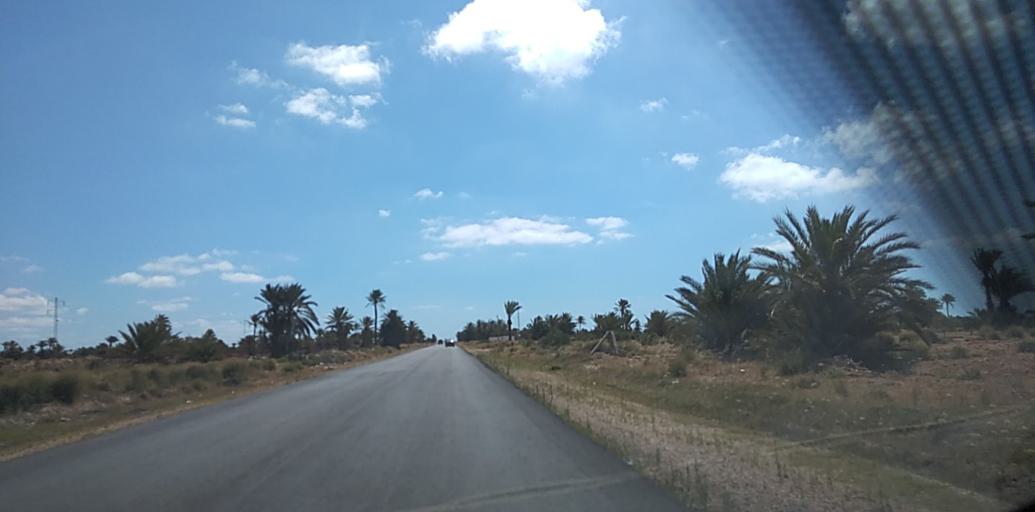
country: TN
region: Safaqis
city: Al Qarmadah
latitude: 34.6593
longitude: 11.1099
